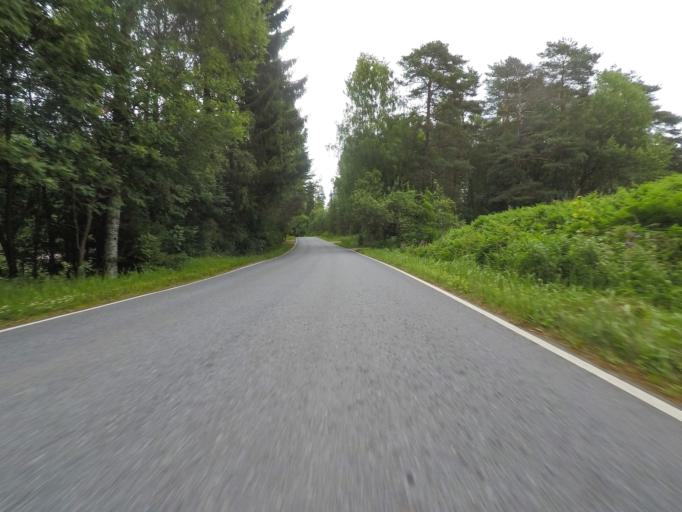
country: FI
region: Varsinais-Suomi
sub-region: Salo
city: Muurla
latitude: 60.3329
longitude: 23.2923
